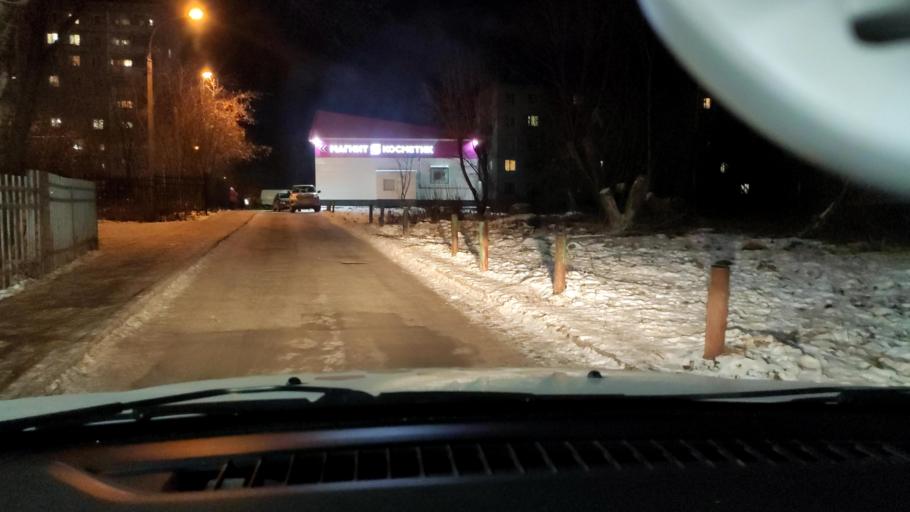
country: RU
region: Perm
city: Kultayevo
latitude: 58.0155
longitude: 55.9771
